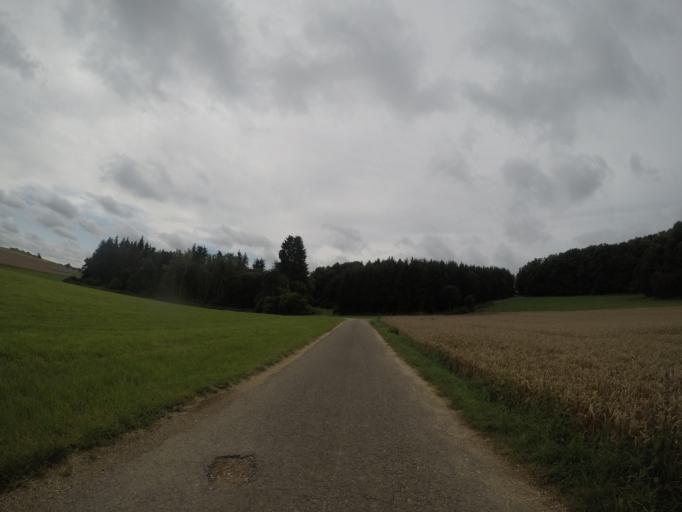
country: DE
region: Baden-Wuerttemberg
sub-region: Tuebingen Region
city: Laichingen
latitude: 48.4665
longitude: 9.6462
